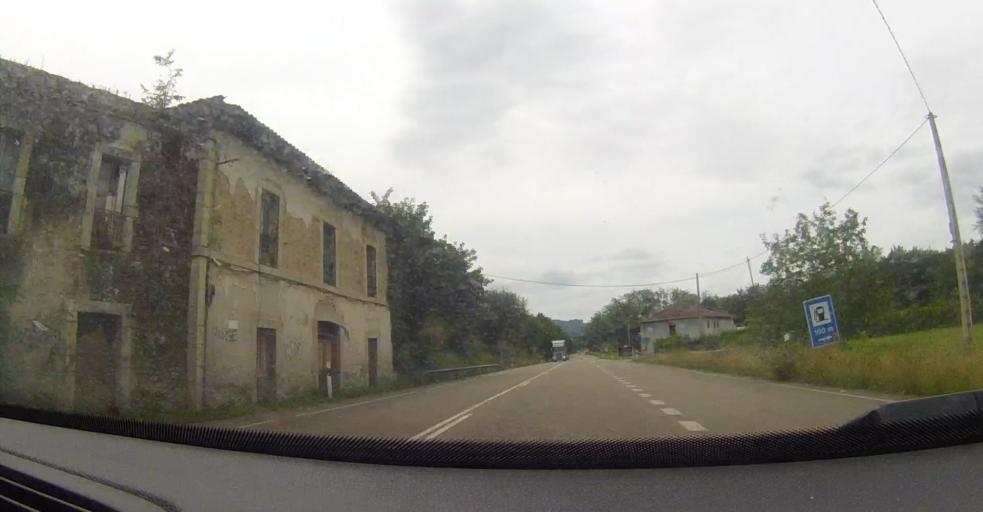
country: ES
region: Asturias
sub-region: Province of Asturias
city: Pilona
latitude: 43.3655
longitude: -5.2702
